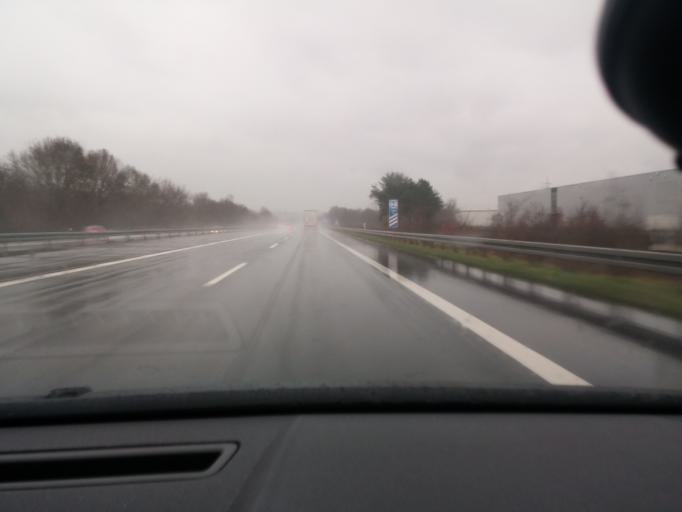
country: DE
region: Bavaria
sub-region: Regierungsbezirk Unterfranken
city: Alzenau in Unterfranken
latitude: 50.0527
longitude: 9.0482
